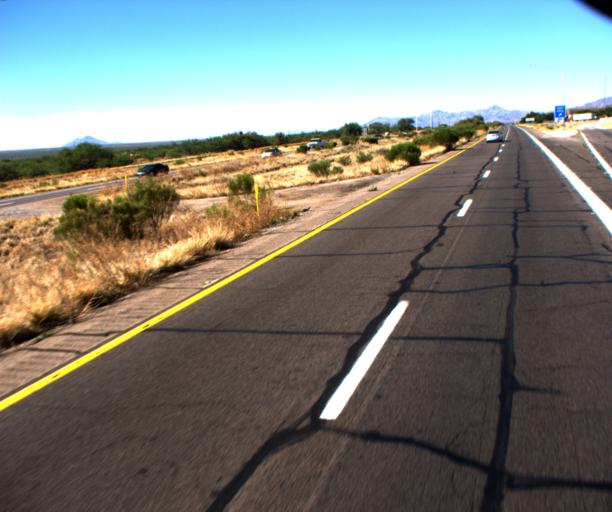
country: US
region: Arizona
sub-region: Pima County
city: Arivaca Junction
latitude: 31.7745
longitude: -111.0315
